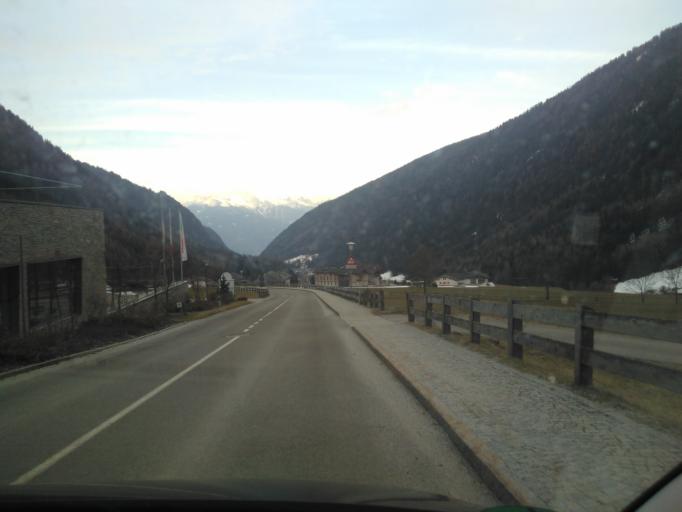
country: IT
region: Trentino-Alto Adige
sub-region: Bolzano
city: Fortezza
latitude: 46.8388
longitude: 11.6271
